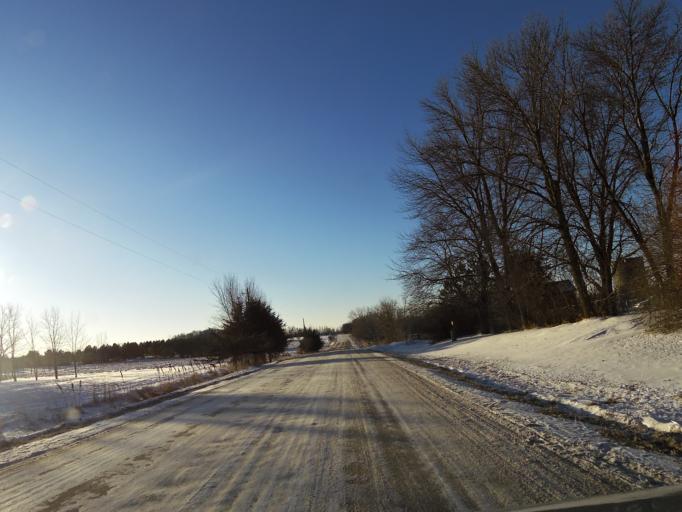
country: US
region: Minnesota
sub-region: Scott County
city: Jordan
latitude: 44.6516
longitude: -93.5163
